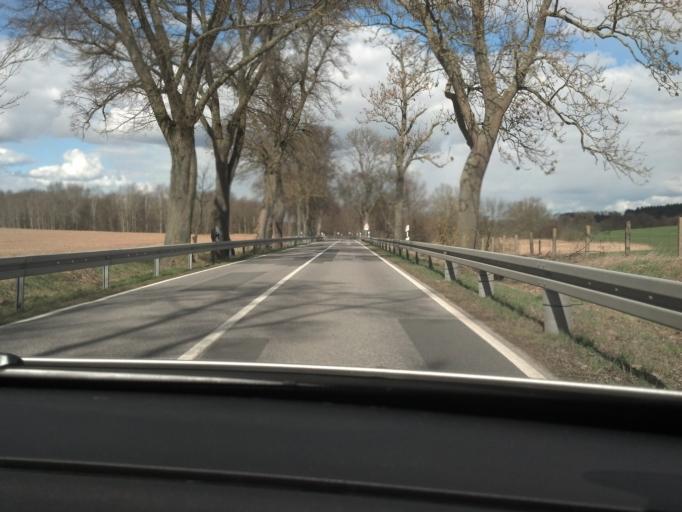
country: DE
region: Mecklenburg-Vorpommern
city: Loitz
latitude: 53.4073
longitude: 13.3645
